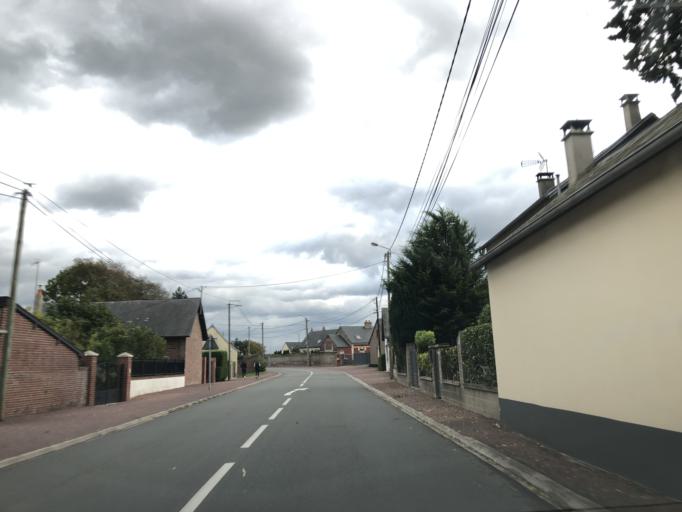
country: FR
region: Picardie
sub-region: Departement de la Somme
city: Pende
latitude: 50.1557
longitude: 1.5509
